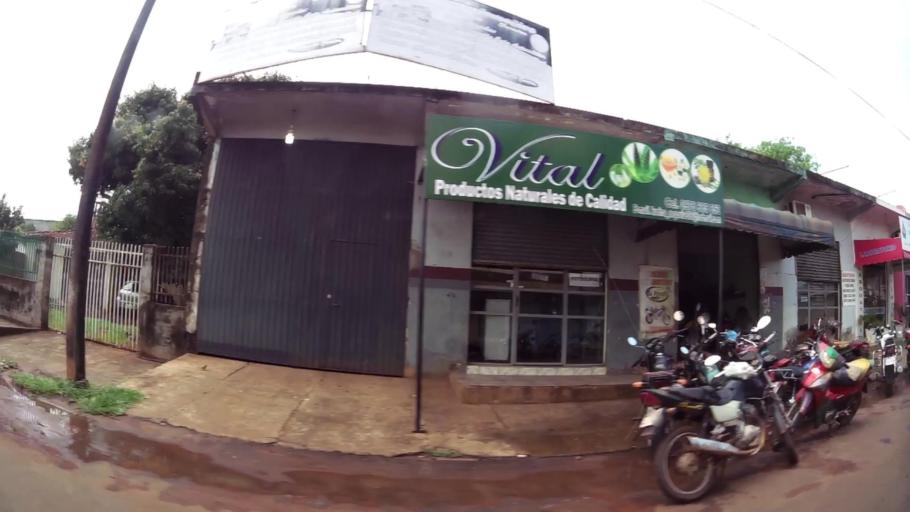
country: PY
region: Alto Parana
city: Ciudad del Este
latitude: -25.5064
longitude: -54.6675
